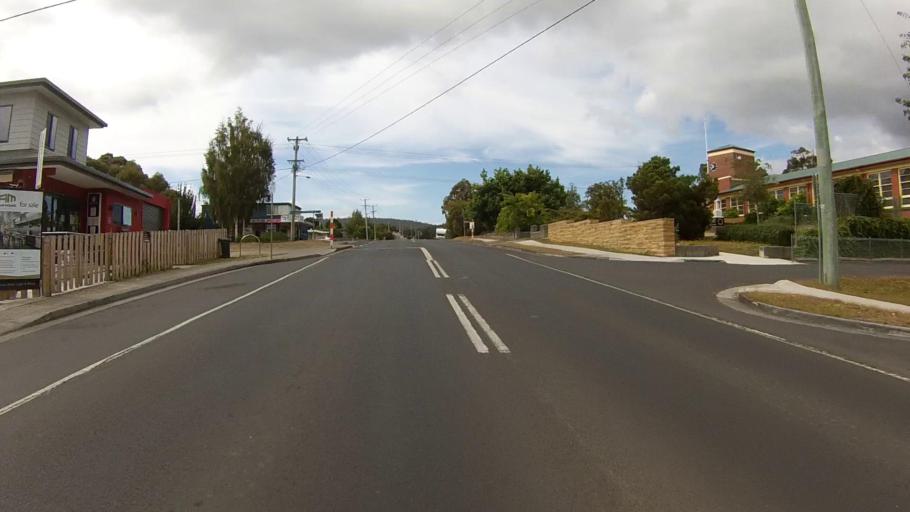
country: AU
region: Tasmania
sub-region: Kingborough
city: Margate
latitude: -43.0657
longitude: 147.2549
